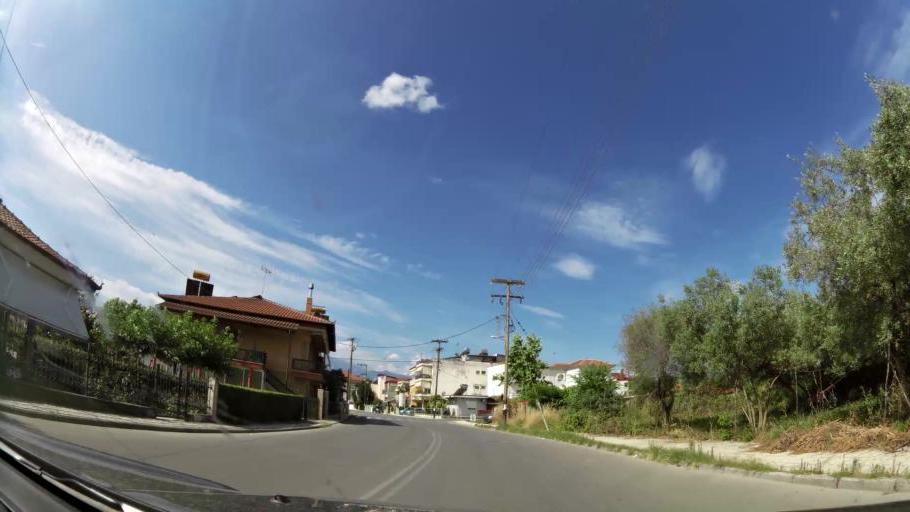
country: GR
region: Central Macedonia
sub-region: Nomos Pierias
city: Katerini
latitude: 40.2773
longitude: 22.4929
